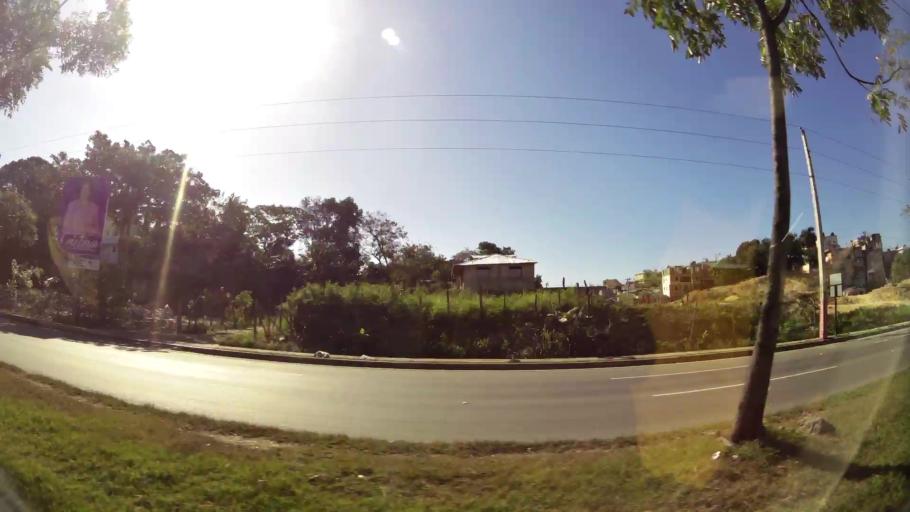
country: DO
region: Nacional
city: Bella Vista
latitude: 18.4508
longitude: -69.9864
